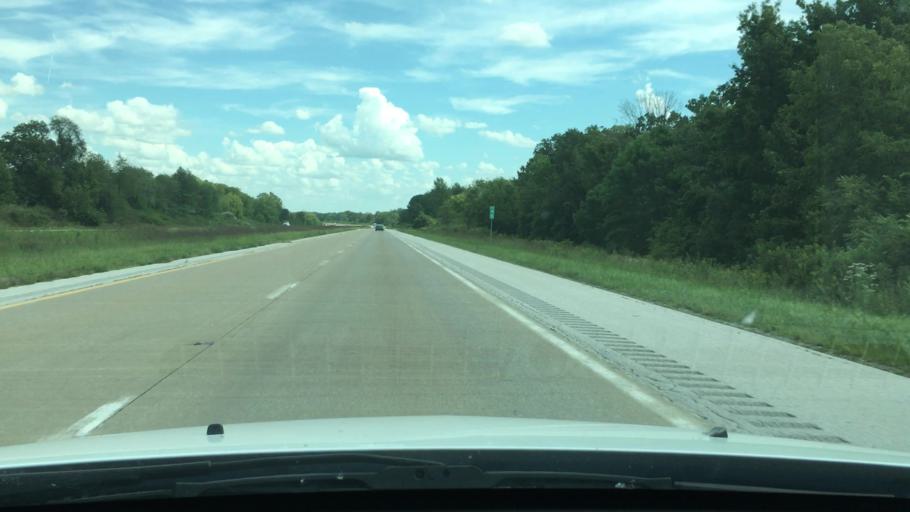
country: US
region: Illinois
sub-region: Scott County
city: Winchester
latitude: 39.6828
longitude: -90.5319
